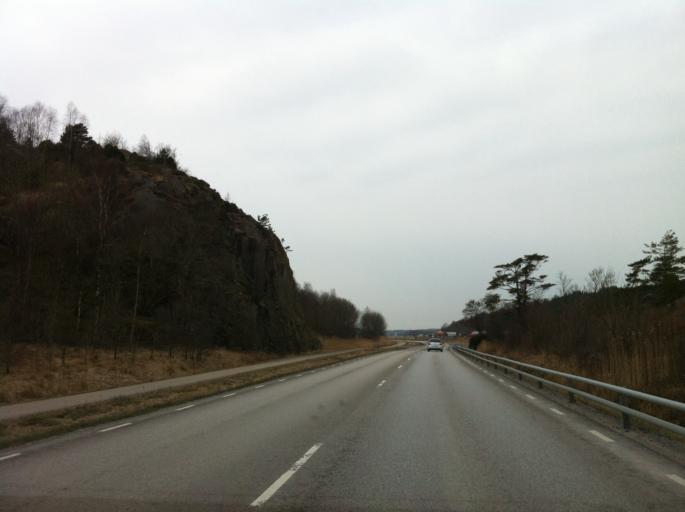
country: SE
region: Vaestra Goetaland
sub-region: Orust
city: Henan
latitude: 58.2222
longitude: 11.6870
